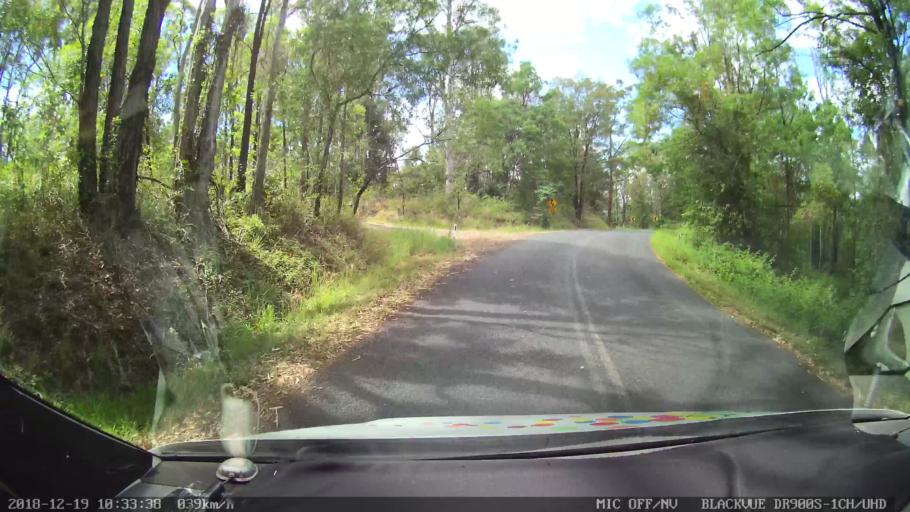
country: AU
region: New South Wales
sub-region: Lismore Municipality
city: Larnook
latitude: -28.5782
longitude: 153.1264
